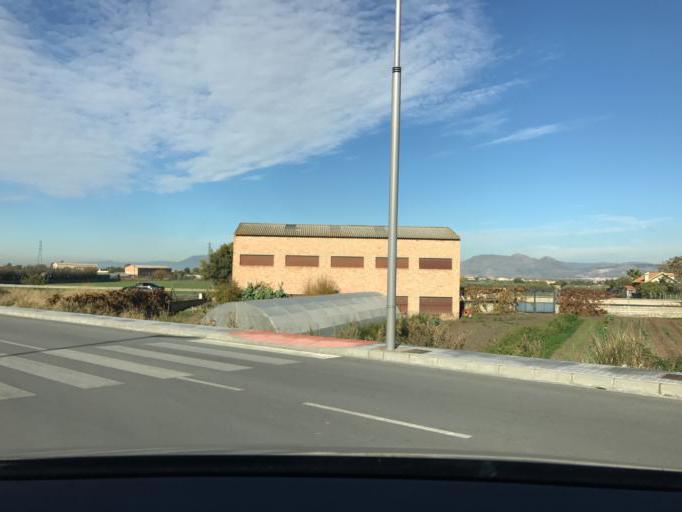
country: ES
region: Andalusia
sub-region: Provincia de Granada
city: Churriana de la Vega
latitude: 37.1506
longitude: -3.6518
